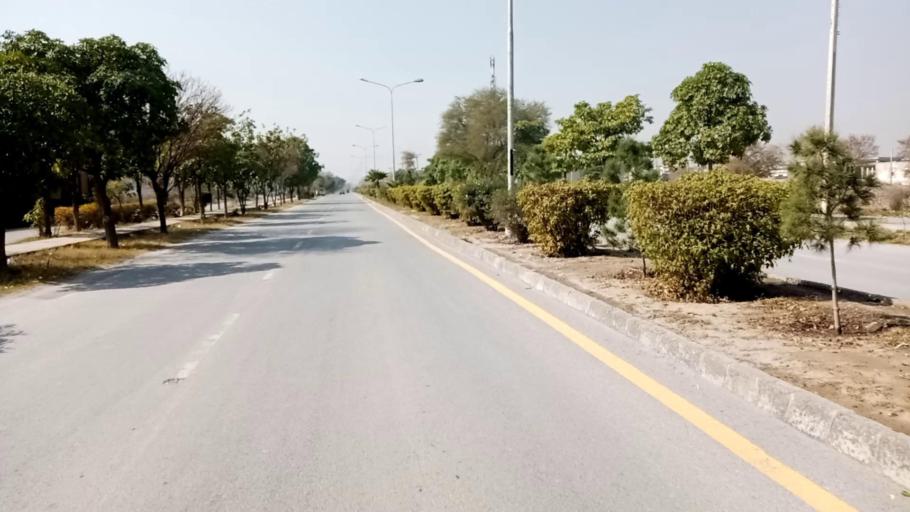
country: PK
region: Khyber Pakhtunkhwa
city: Peshawar
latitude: 33.9632
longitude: 71.4206
